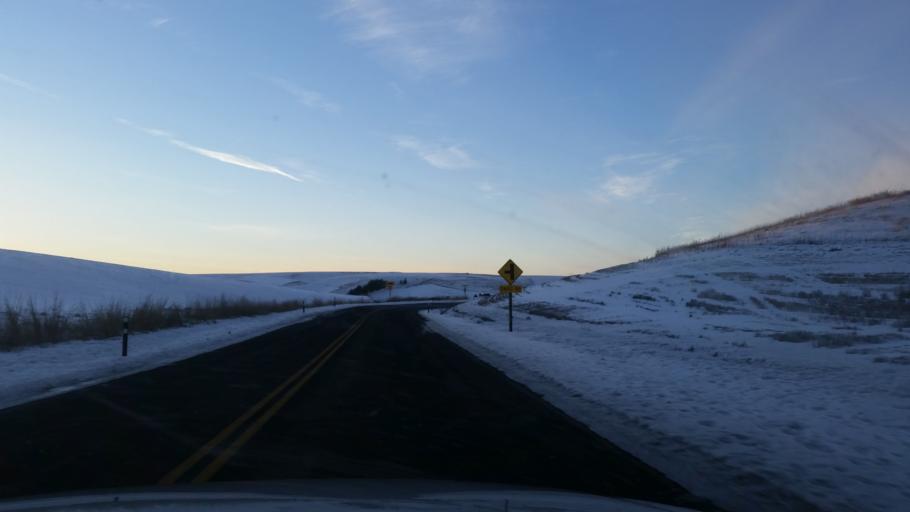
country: US
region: Washington
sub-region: Spokane County
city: Cheney
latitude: 47.1573
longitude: -117.8687
